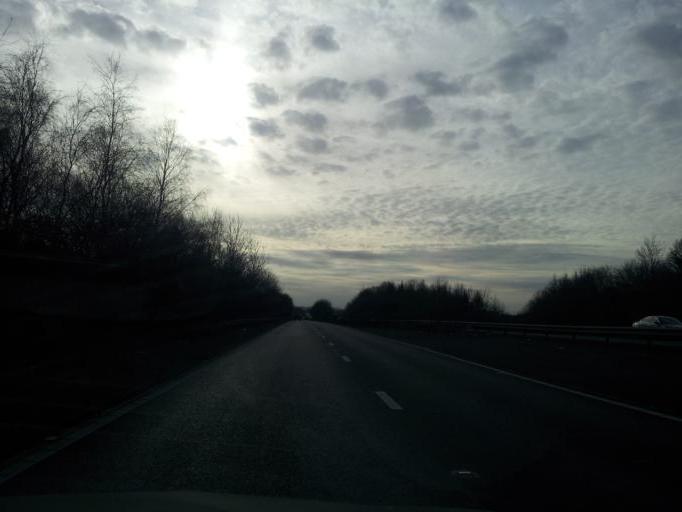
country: GB
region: England
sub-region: District of Rutland
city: Tickencote
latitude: 52.6920
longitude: -0.5627
